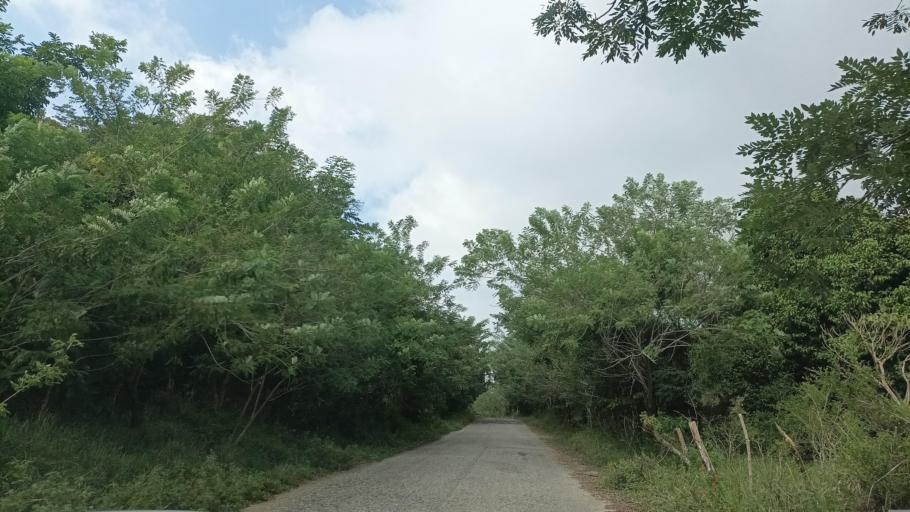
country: MX
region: Veracruz
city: Allende
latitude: 18.0987
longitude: -94.2938
